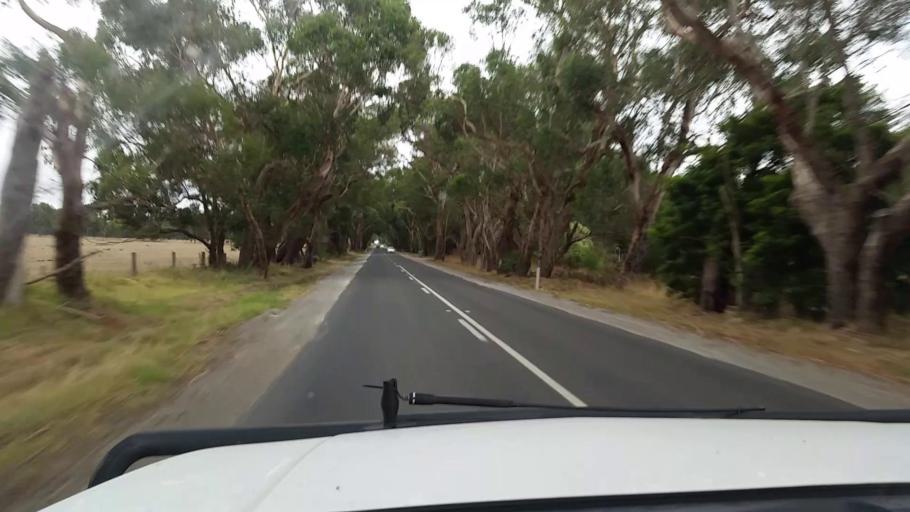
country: AU
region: Victoria
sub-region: Mornington Peninsula
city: Balnarring
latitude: -38.3289
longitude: 145.1457
